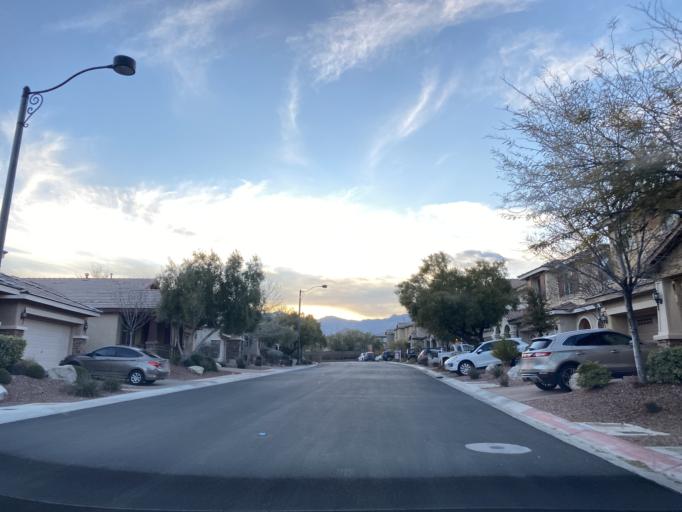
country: US
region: Nevada
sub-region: Clark County
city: Summerlin South
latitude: 36.3018
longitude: -115.3246
